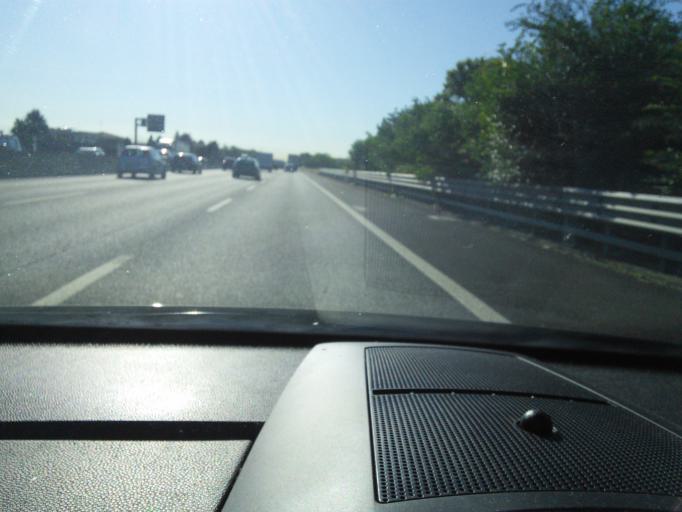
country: IT
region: Lombardy
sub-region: Citta metropolitana di Milano
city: Cerro Maggiore
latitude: 45.5989
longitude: 8.9549
